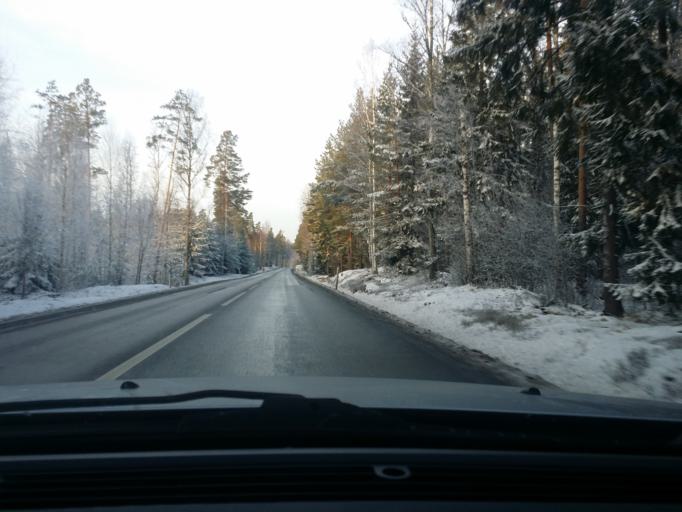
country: SE
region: OErebro
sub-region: Lindesbergs Kommun
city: Frovi
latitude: 59.5102
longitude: 15.3540
